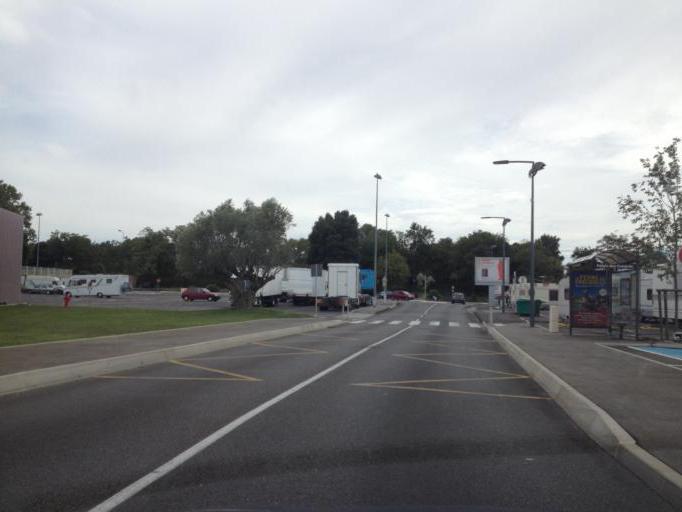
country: FR
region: Rhone-Alpes
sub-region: Departement de la Drome
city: Montelimar
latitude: 44.5551
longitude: 4.7440
